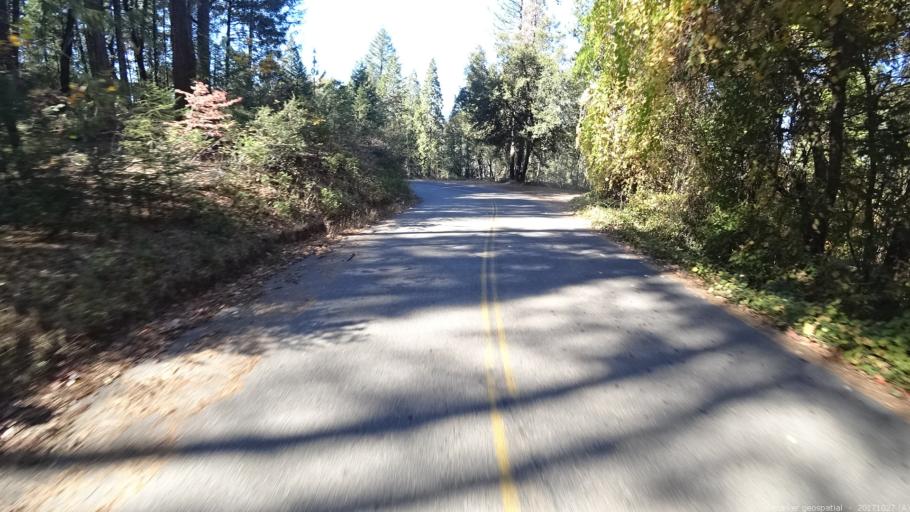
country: US
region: California
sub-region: Shasta County
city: Shingletown
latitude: 40.7376
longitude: -121.9516
